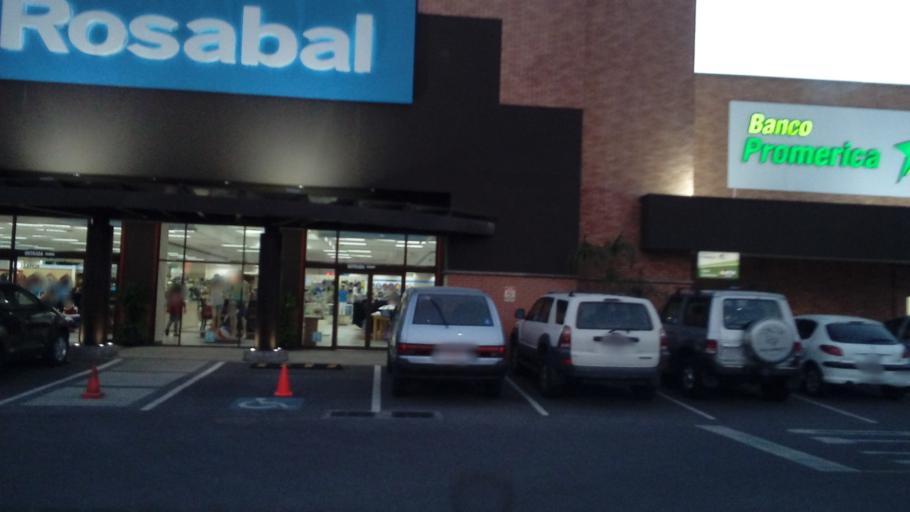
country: CR
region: Heredia
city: Heredia
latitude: 9.9882
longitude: -84.1115
